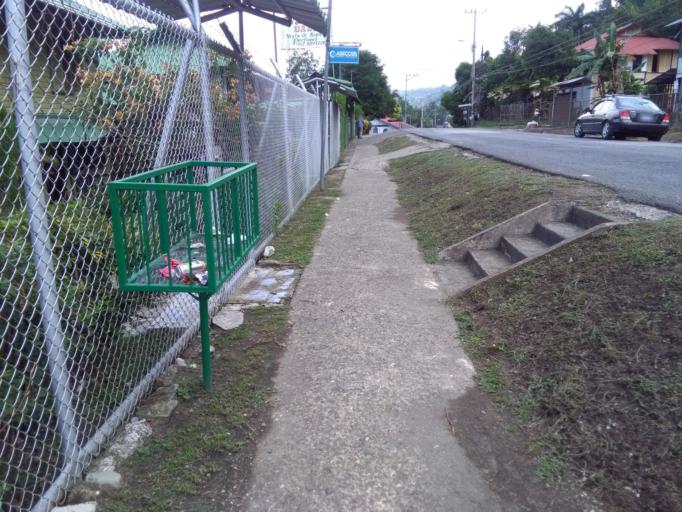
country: CR
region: Puntarenas
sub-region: Canton de Golfito
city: Golfito
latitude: 8.6407
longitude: -83.1685
